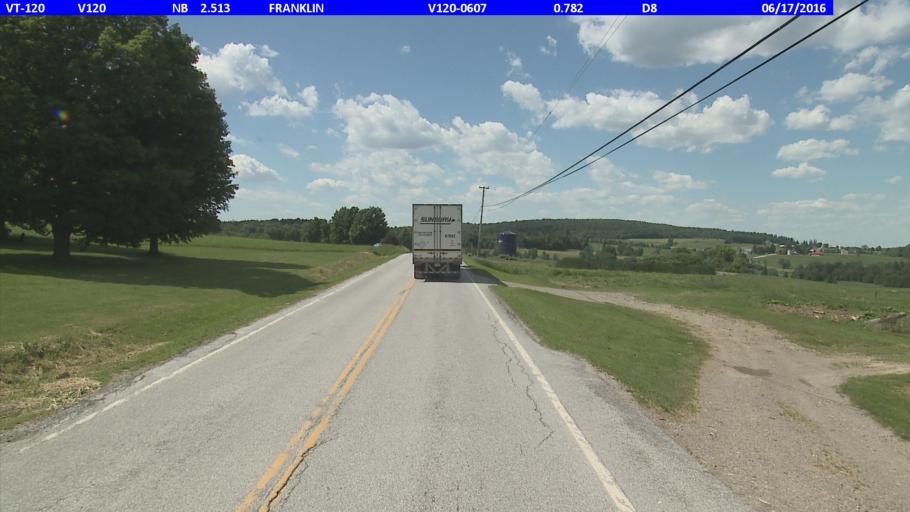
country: US
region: Vermont
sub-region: Franklin County
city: Enosburg Falls
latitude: 44.9451
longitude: -72.9017
